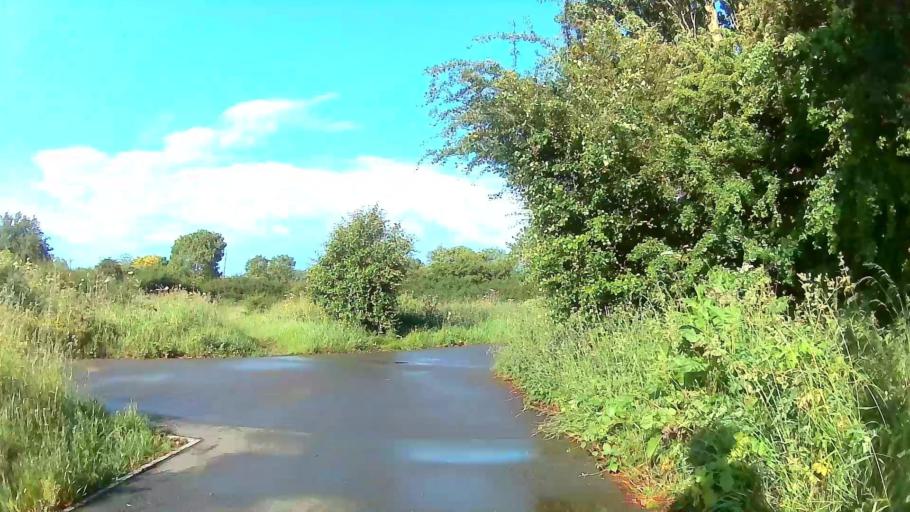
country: GB
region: England
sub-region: Essex
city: Writtle
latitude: 51.7376
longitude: 0.4389
